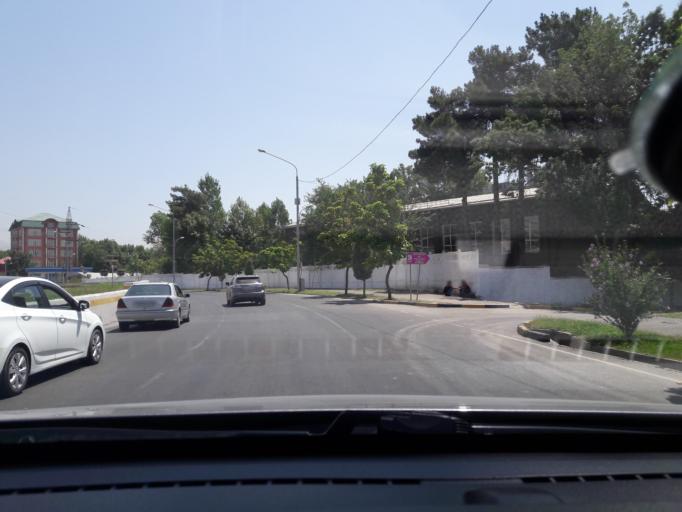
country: TJ
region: Dushanbe
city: Dushanbe
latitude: 38.5934
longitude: 68.7517
